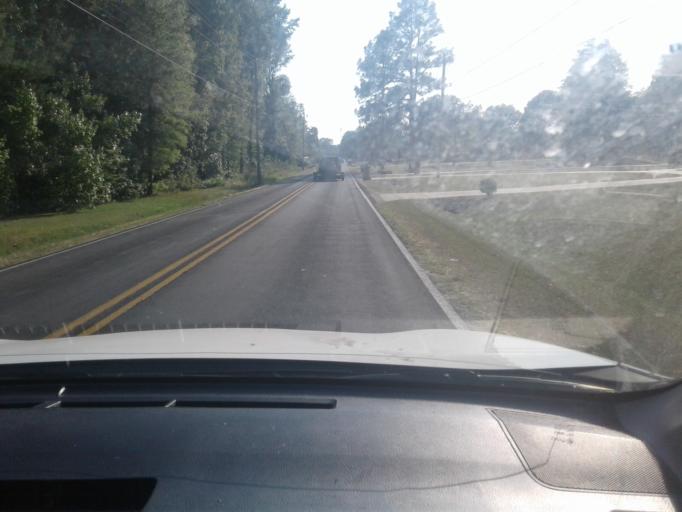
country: US
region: North Carolina
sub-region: Harnett County
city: Erwin
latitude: 35.3228
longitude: -78.6715
